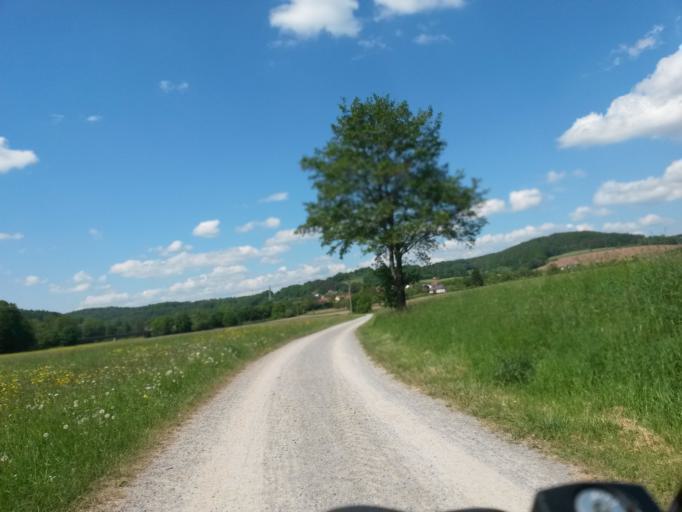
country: DE
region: Bavaria
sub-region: Regierungsbezirk Unterfranken
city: Bad Bocklet
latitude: 50.2548
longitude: 10.0737
